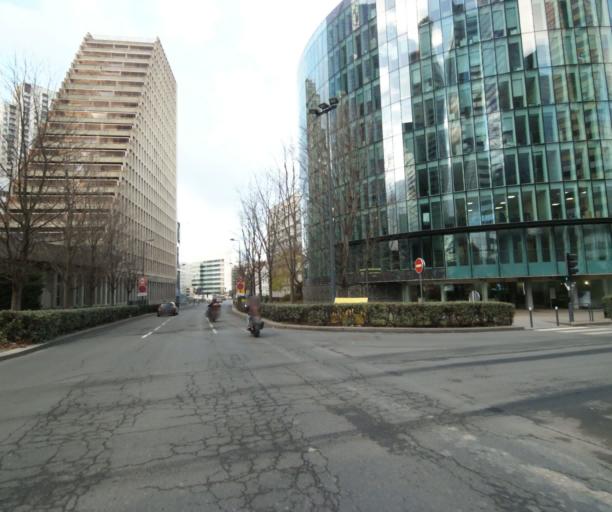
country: FR
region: Ile-de-France
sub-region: Departement des Hauts-de-Seine
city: La Defense
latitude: 48.8928
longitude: 2.2453
